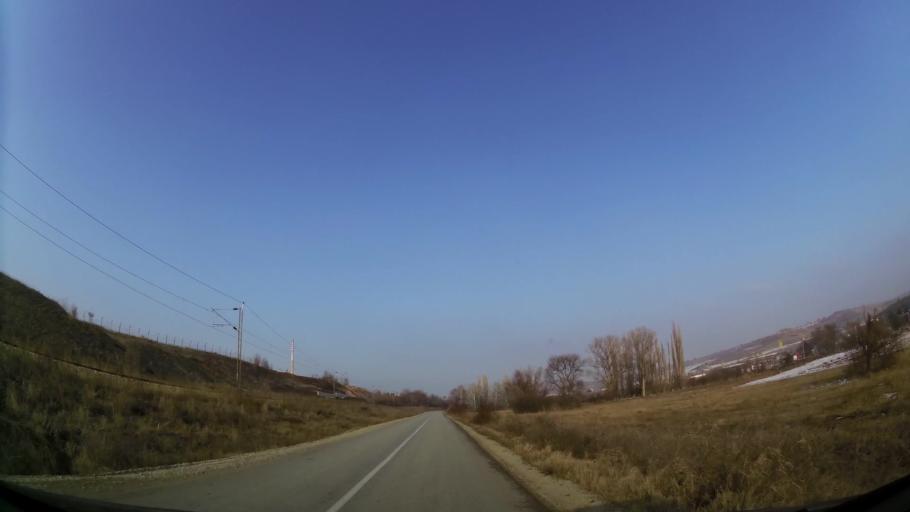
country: MK
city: Miladinovci
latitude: 41.9947
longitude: 21.6562
